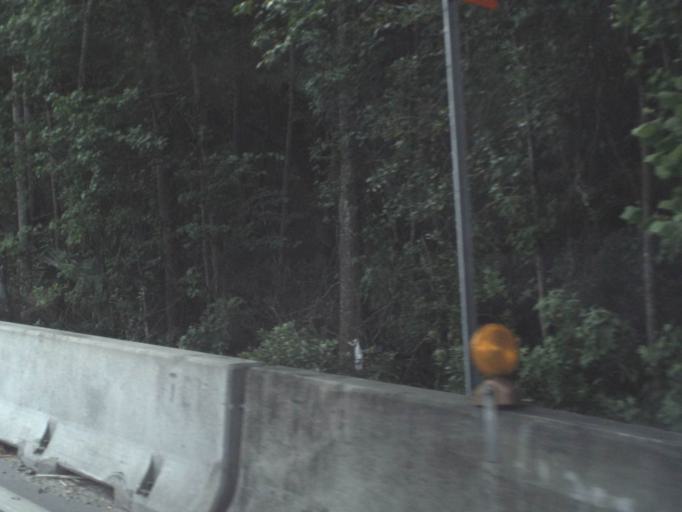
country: US
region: Florida
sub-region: Nassau County
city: Yulee
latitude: 30.6314
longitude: -81.5961
